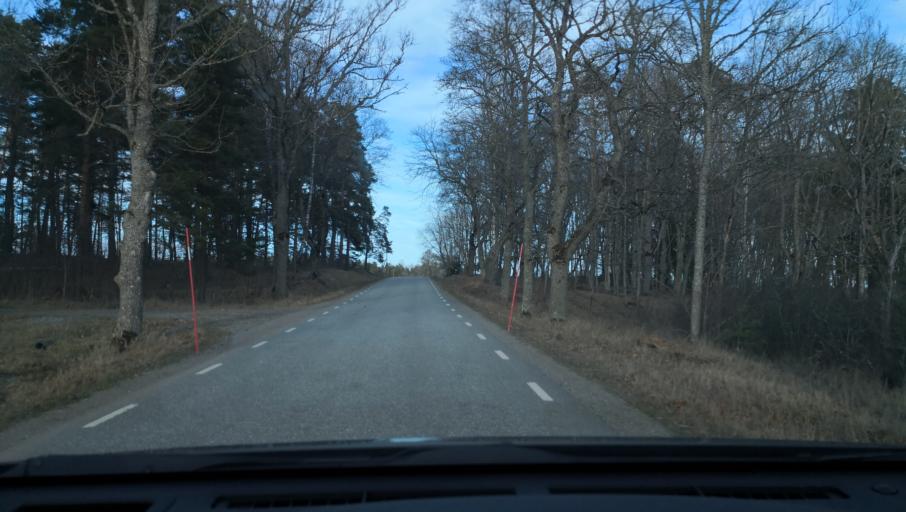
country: SE
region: Uppsala
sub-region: Enkopings Kommun
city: Grillby
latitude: 59.5470
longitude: 17.2119
